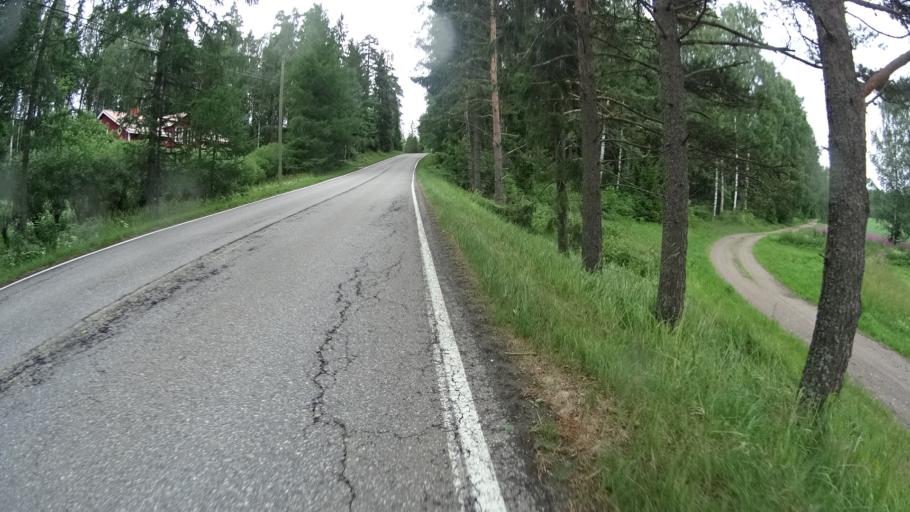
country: FI
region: Uusimaa
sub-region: Helsinki
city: Karkkila
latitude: 60.5690
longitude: 24.3214
